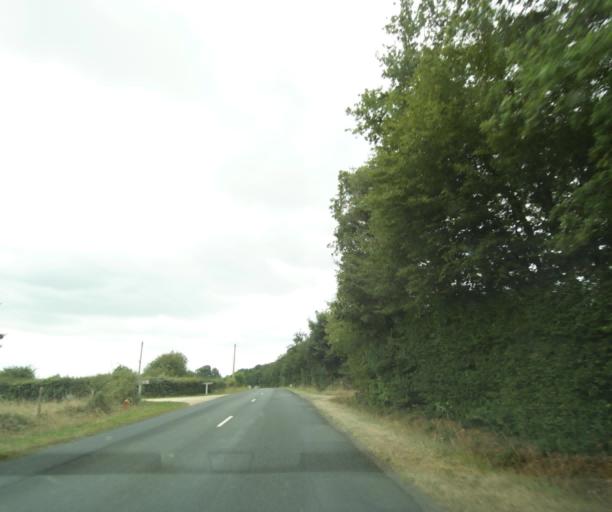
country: FR
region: Pays de la Loire
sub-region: Departement de la Sarthe
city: Precigne
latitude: 47.7939
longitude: -0.3208
